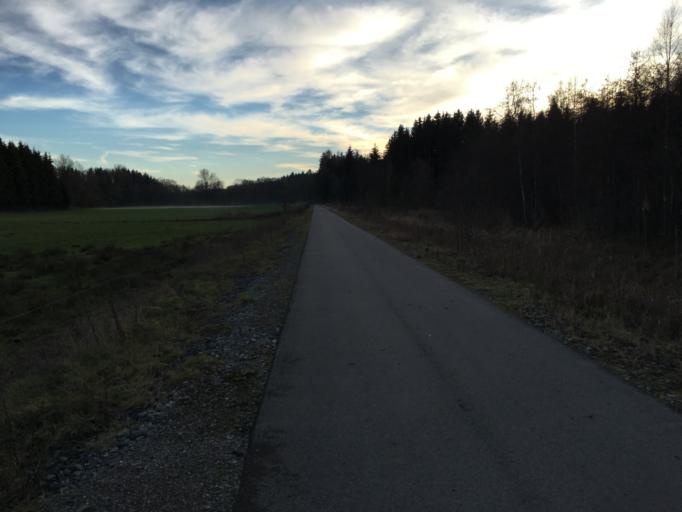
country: DE
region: Bavaria
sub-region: Swabia
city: Westerheim
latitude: 47.9977
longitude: 10.2889
